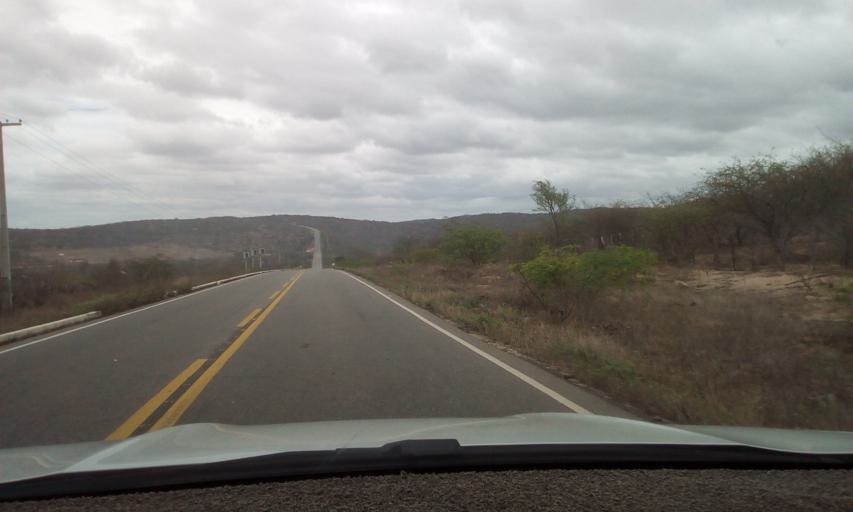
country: BR
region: Paraiba
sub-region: Picui
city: Picui
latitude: -6.5405
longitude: -36.3024
